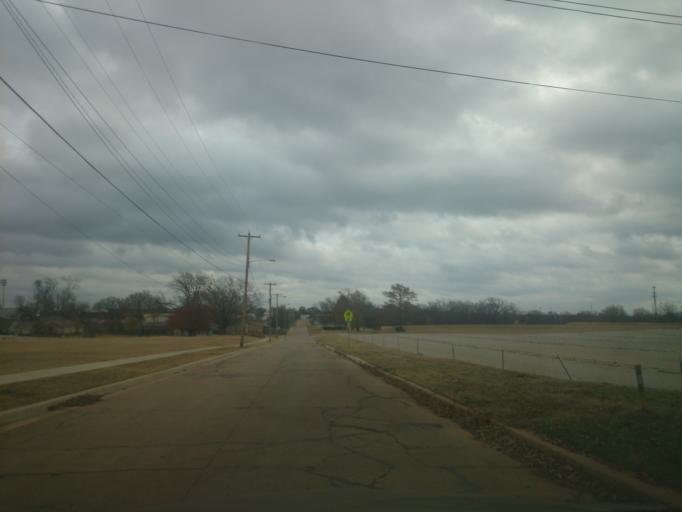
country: US
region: Oklahoma
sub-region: Payne County
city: Stillwater
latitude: 36.1341
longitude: -97.0690
